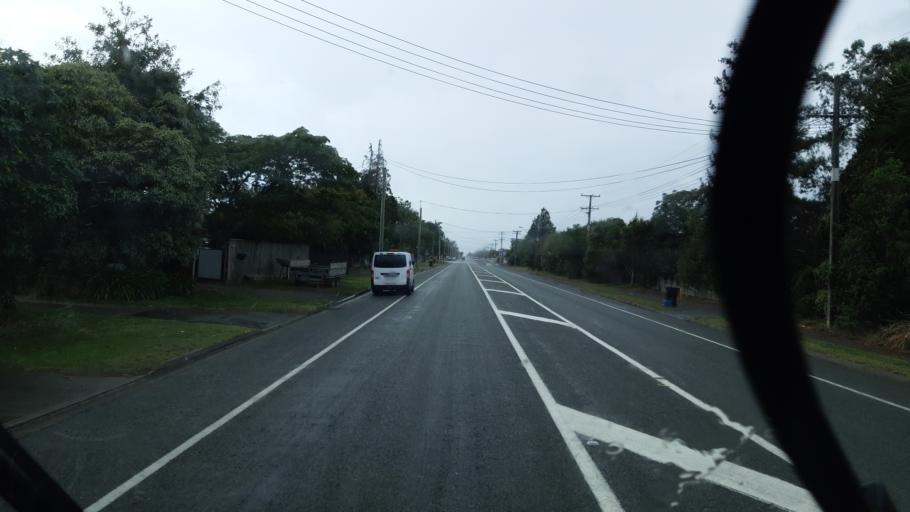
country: NZ
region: Tasman
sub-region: Tasman District
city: Richmond
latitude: -41.3555
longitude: 173.1516
